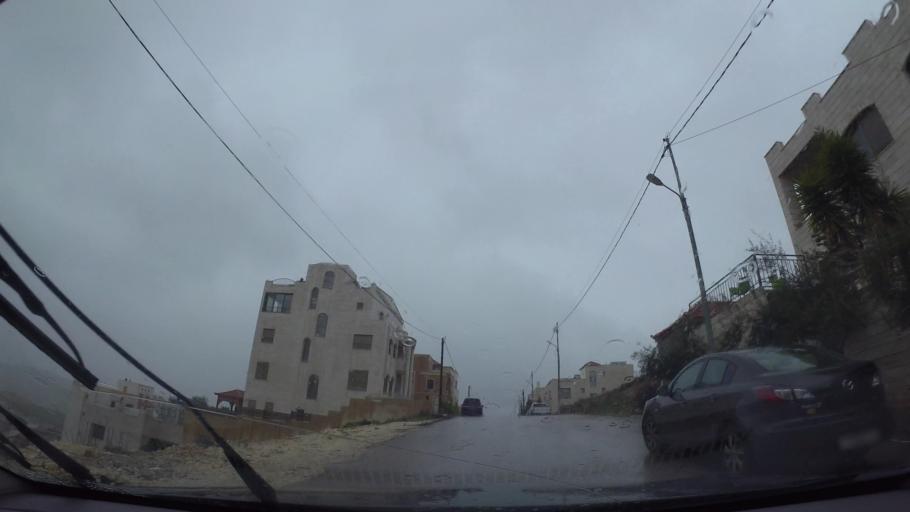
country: JO
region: Amman
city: Al Jubayhah
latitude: 32.0100
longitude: 35.8988
